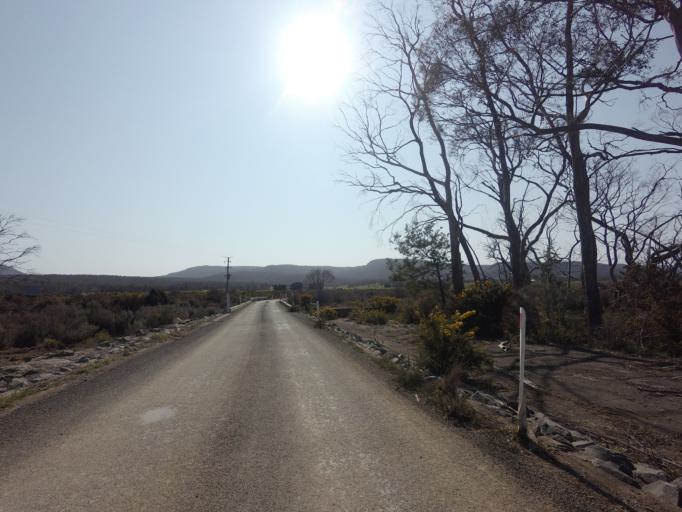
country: AU
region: Tasmania
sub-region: Break O'Day
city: St Helens
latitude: -41.8148
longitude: 147.9414
